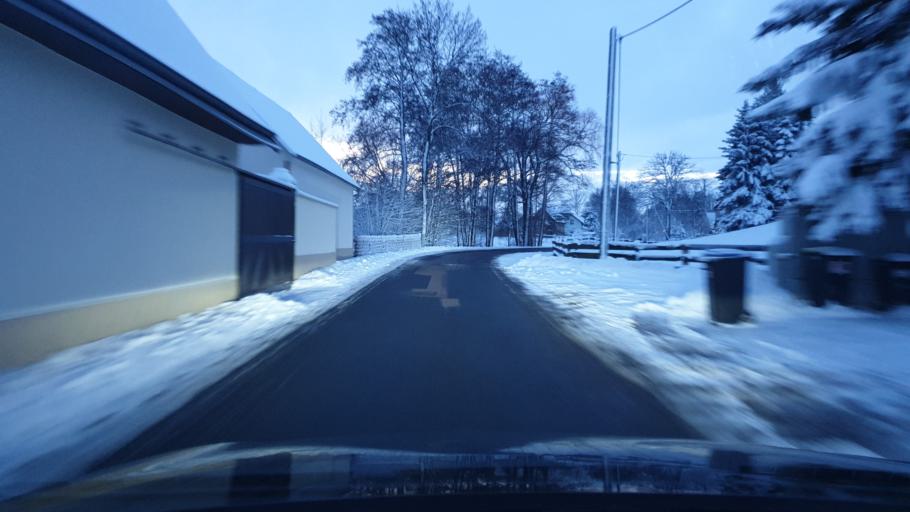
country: DE
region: Saxony
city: Altmittweida
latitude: 50.9872
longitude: 12.9292
